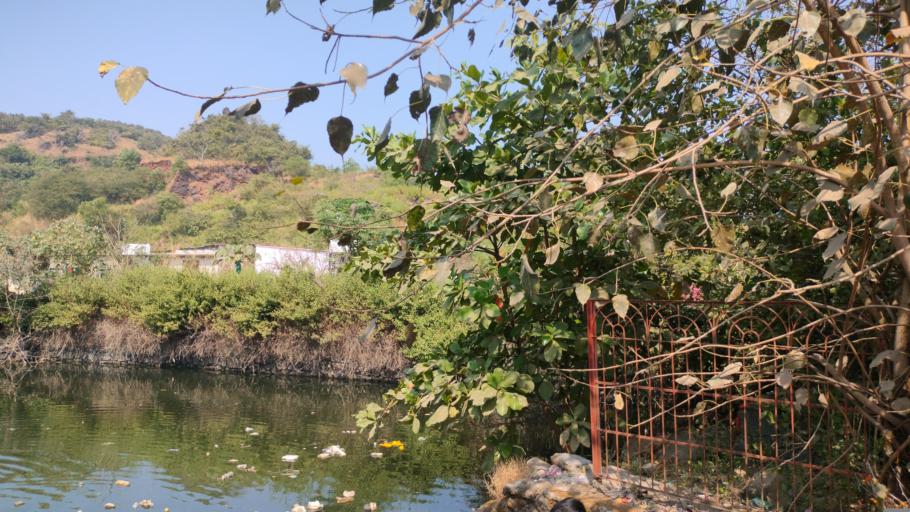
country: IN
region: Maharashtra
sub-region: Thane
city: Bhayandar
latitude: 19.3551
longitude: 72.8847
